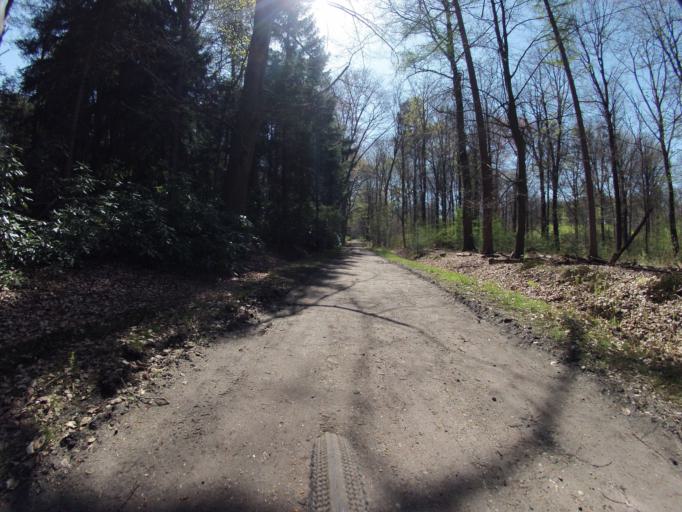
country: NL
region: Overijssel
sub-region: Gemeente Oldenzaal
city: Oldenzaal
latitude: 52.2760
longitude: 6.9164
